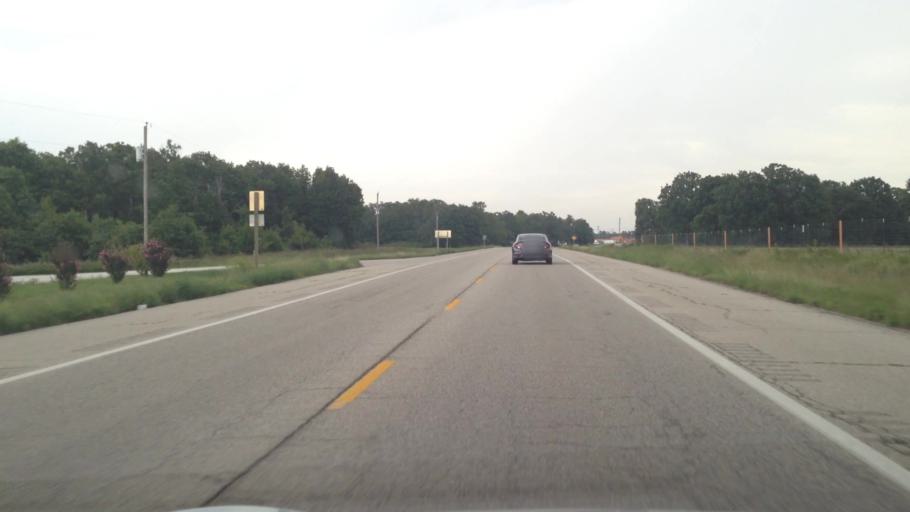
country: US
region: Kansas
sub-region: Cherokee County
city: Galena
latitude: 37.0081
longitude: -94.6220
